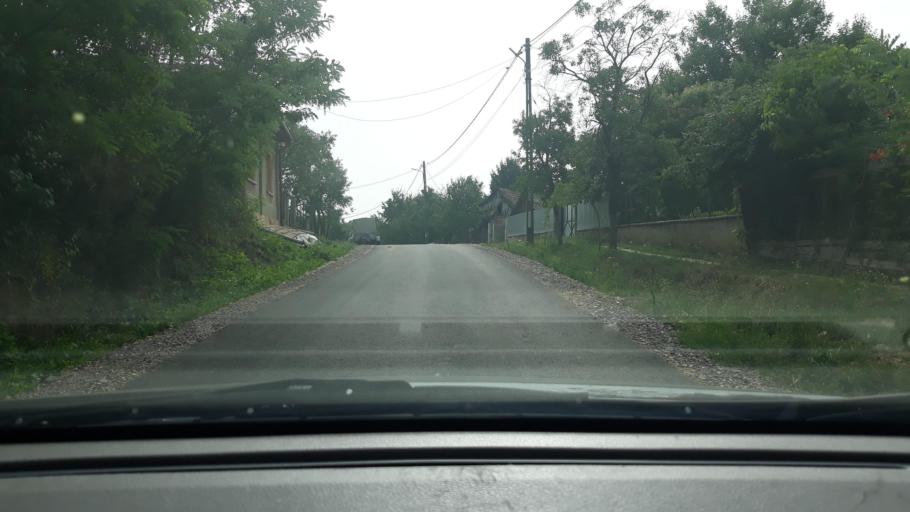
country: RO
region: Bihor
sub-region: Comuna Chislaz
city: Misca
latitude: 47.2655
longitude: 22.2573
